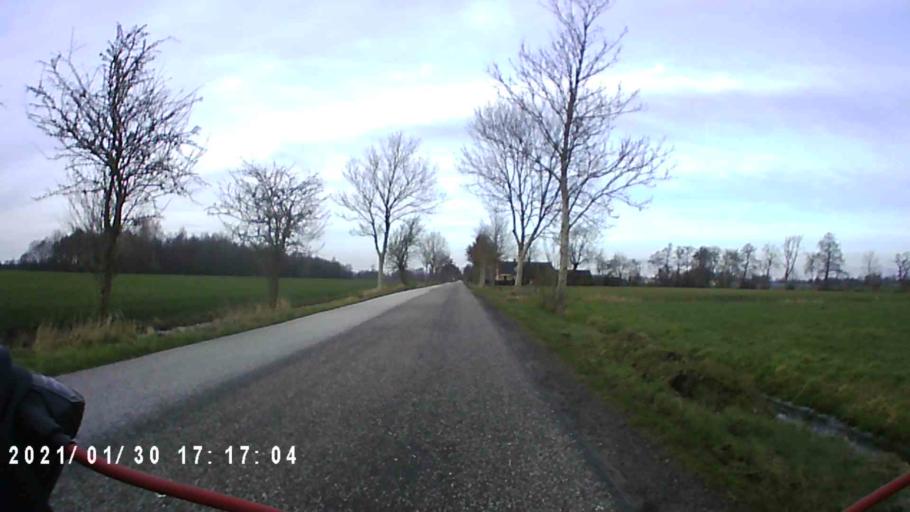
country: NL
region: Groningen
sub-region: Gemeente Leek
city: Leek
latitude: 53.1807
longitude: 6.3593
